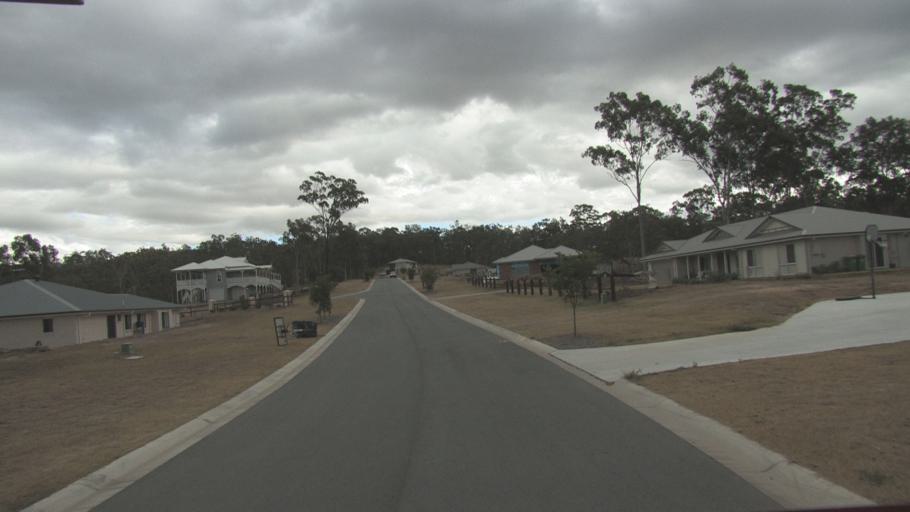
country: AU
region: Queensland
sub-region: Logan
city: Cedar Vale
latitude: -27.8622
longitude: 153.0727
